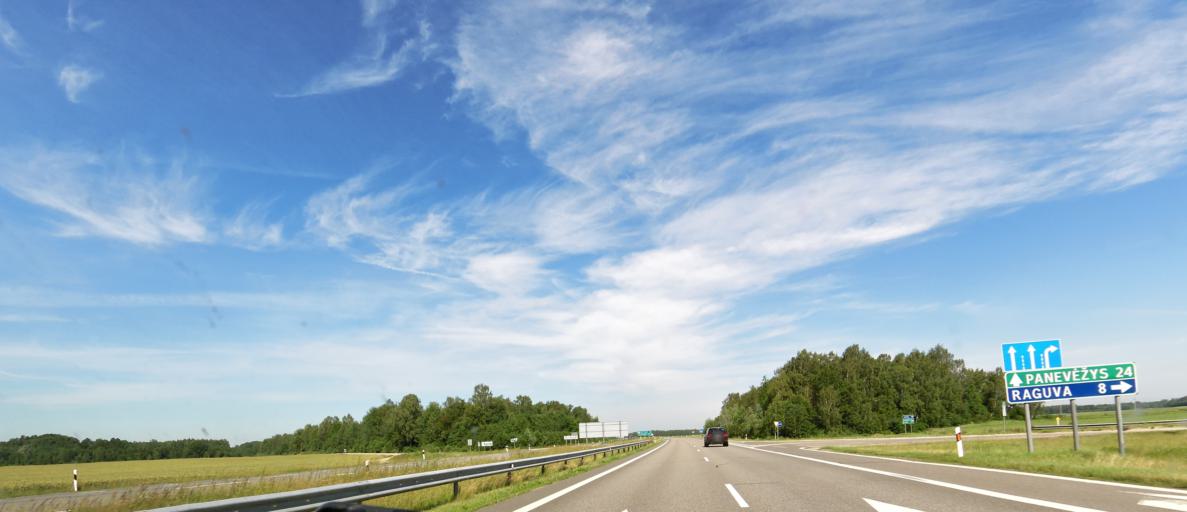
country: LT
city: Ramygala
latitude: 55.5526
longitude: 24.5177
